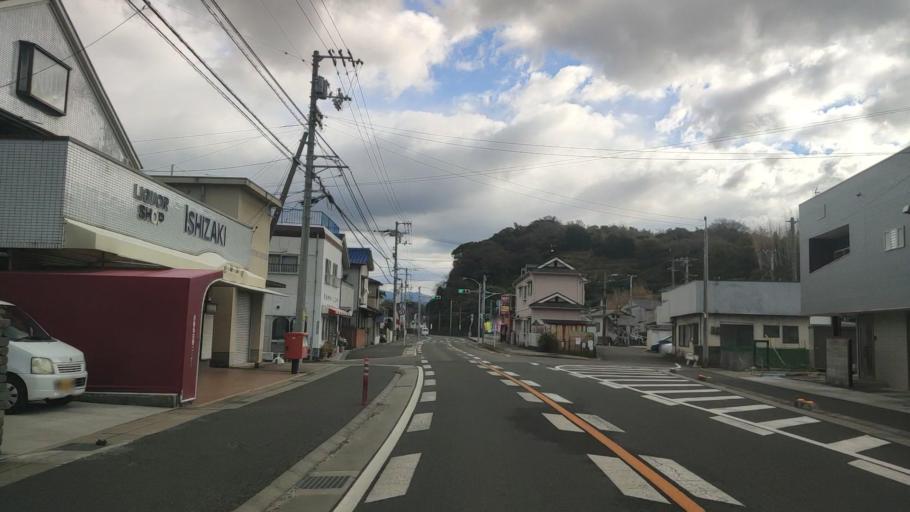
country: JP
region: Ehime
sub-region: Shikoku-chuo Shi
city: Matsuyama
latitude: 33.8698
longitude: 132.7120
